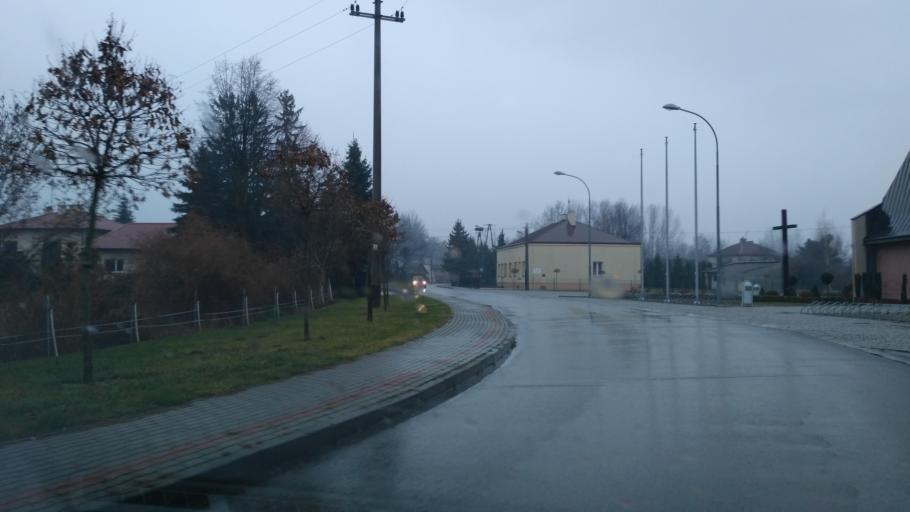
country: PL
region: Subcarpathian Voivodeship
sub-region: Powiat rzeszowski
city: Wolka Podlesna
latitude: 50.0776
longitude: 22.1356
